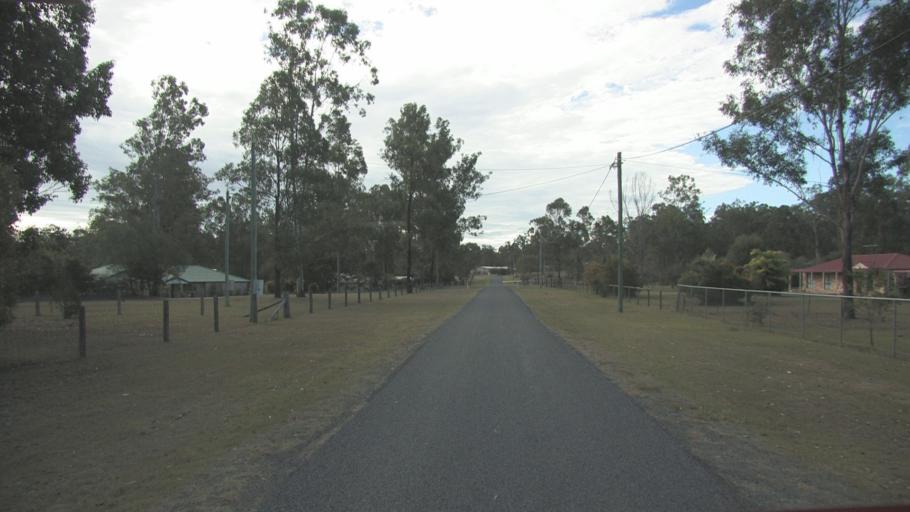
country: AU
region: Queensland
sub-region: Logan
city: North Maclean
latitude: -27.8227
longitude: 153.0487
